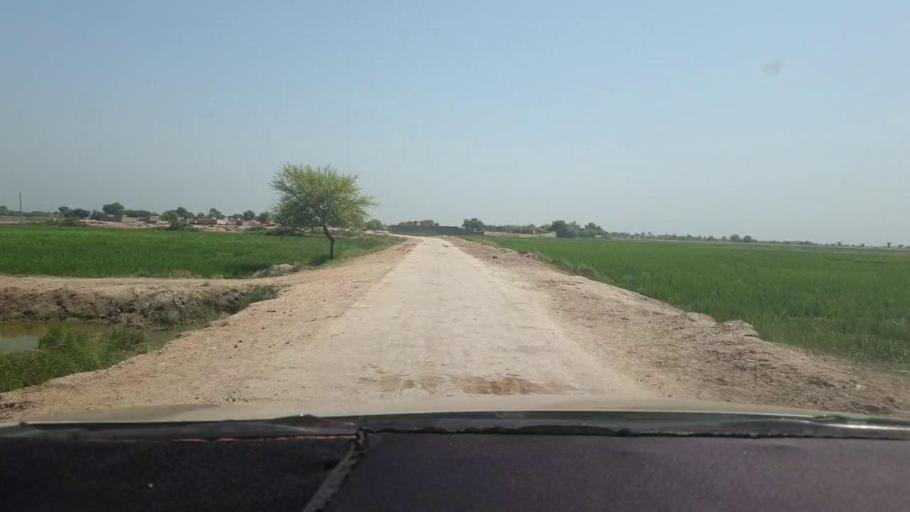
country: PK
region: Sindh
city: Miro Khan
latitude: 27.6736
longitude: 68.0951
